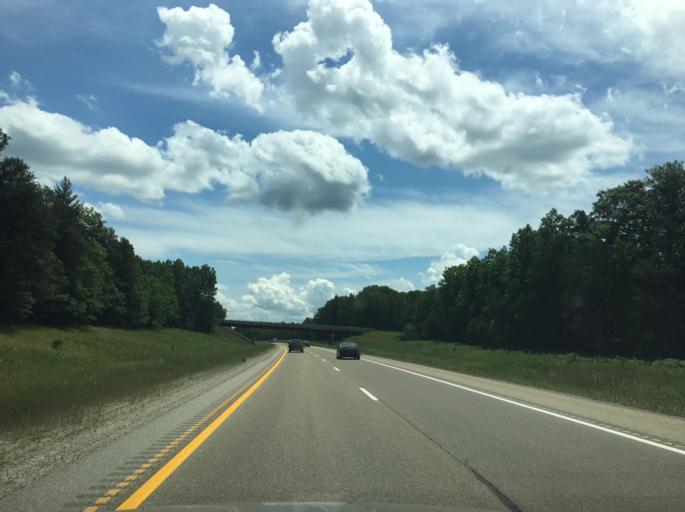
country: US
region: Michigan
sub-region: Crawford County
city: Grayling
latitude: 44.5566
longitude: -84.7069
